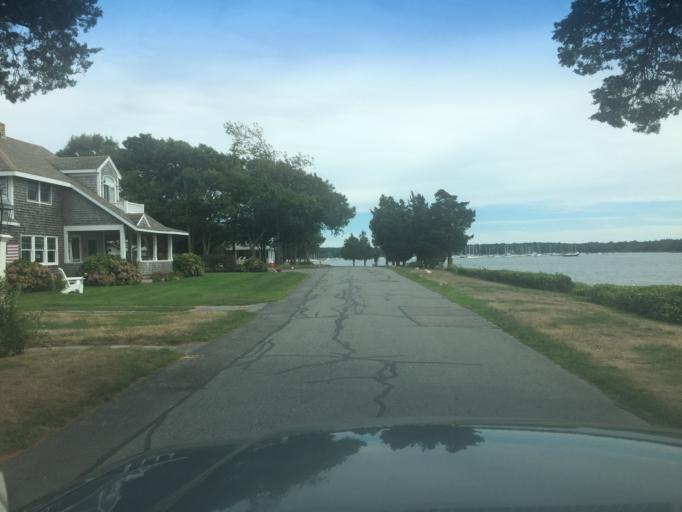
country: US
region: Massachusetts
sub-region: Barnstable County
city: Pocasset
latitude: 41.6824
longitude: -70.6278
